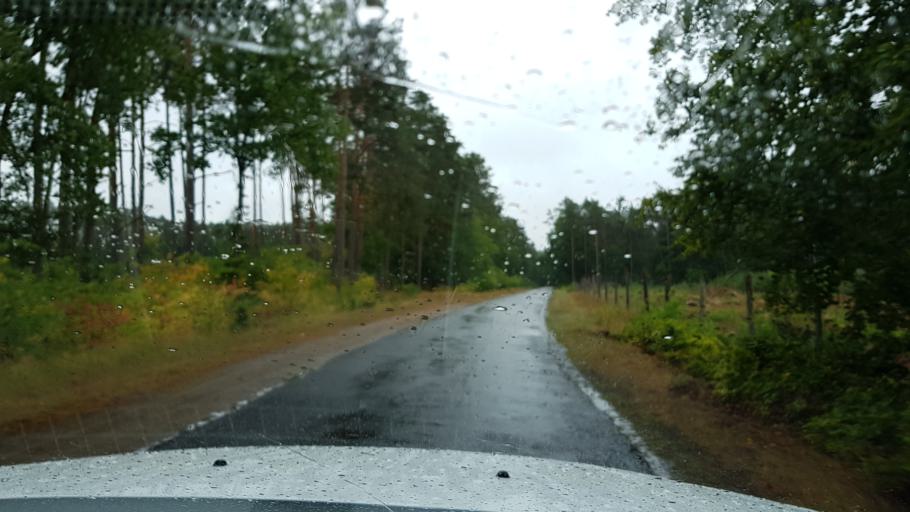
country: DE
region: Brandenburg
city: Schoneberg
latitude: 52.9648
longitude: 14.2035
